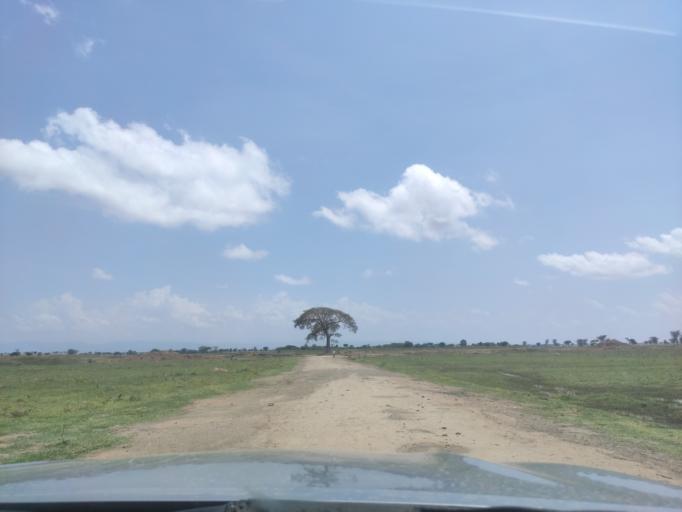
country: ET
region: Oromiya
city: Ziway
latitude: 8.2360
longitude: 38.8769
